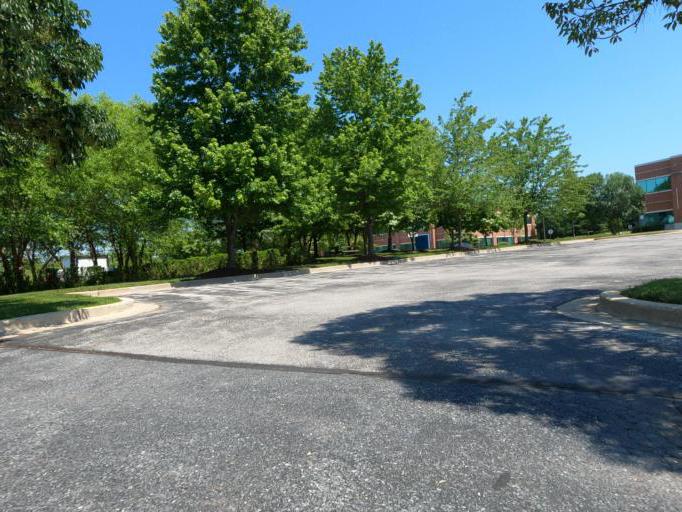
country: US
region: Maryland
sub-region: Montgomery County
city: Germantown
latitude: 39.1930
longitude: -77.2673
